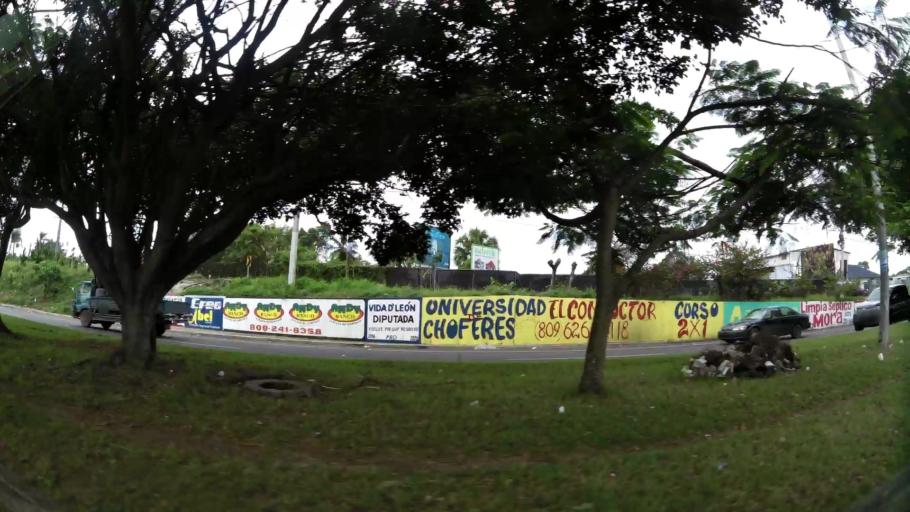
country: DO
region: Santiago
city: Licey al Medio
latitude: 19.4153
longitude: -70.6440
